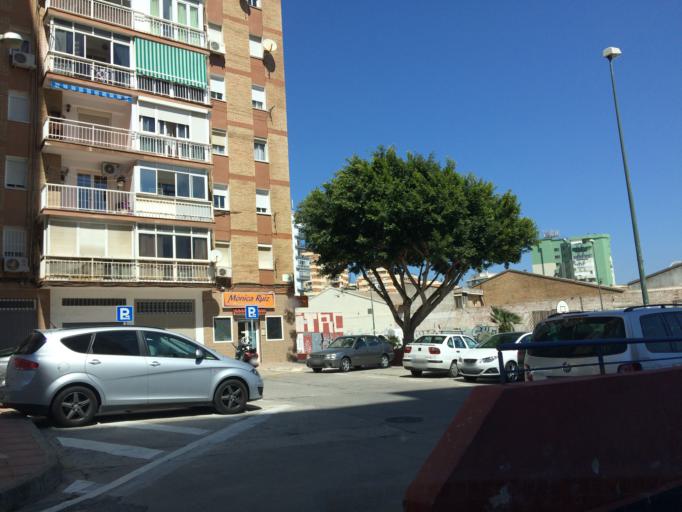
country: ES
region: Andalusia
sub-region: Provincia de Malaga
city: Malaga
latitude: 36.6915
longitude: -4.4532
